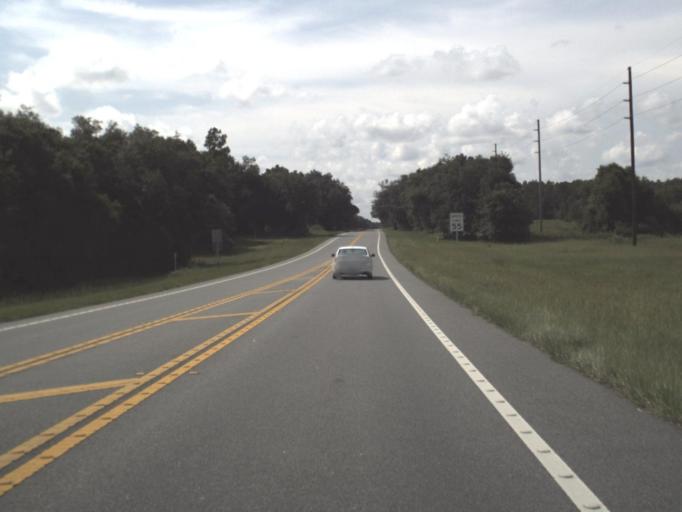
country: US
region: Florida
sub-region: Citrus County
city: Citrus Springs
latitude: 28.9800
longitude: -82.4294
